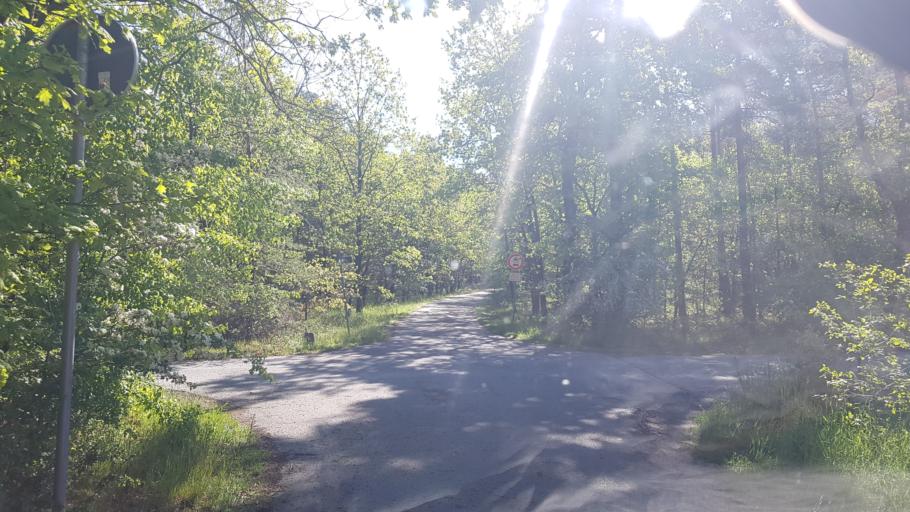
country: DE
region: Brandenburg
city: Grossraschen
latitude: 51.5982
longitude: 13.9578
